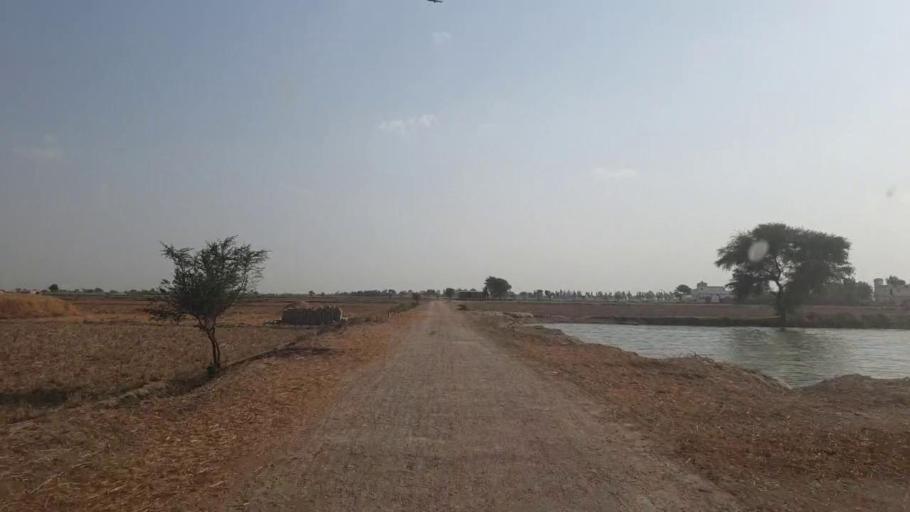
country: PK
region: Sindh
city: Kario
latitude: 24.5555
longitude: 68.5084
